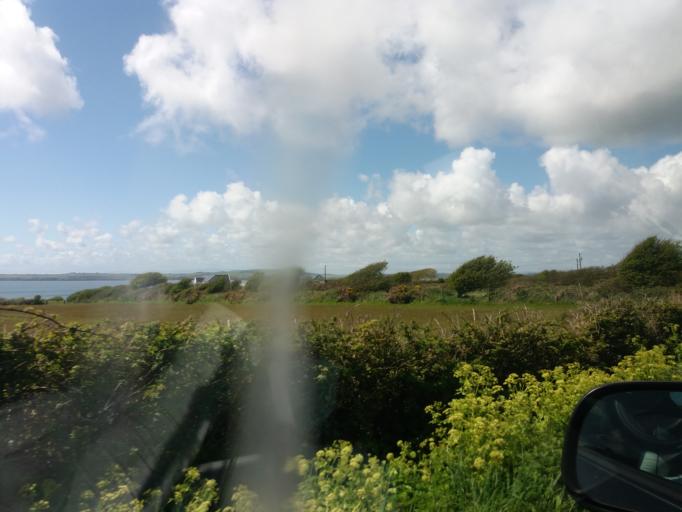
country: IE
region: Munster
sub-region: Waterford
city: Dunmore East
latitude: 52.1658
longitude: -6.8943
